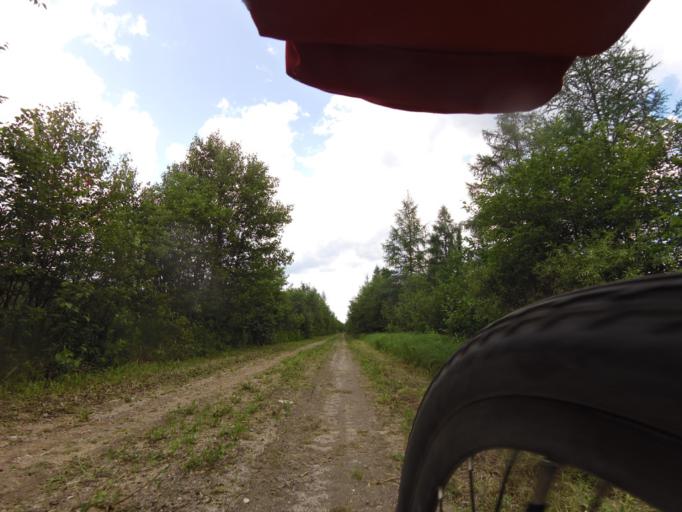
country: CA
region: Quebec
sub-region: Outaouais
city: Wakefield
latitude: 45.9163
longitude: -76.0449
